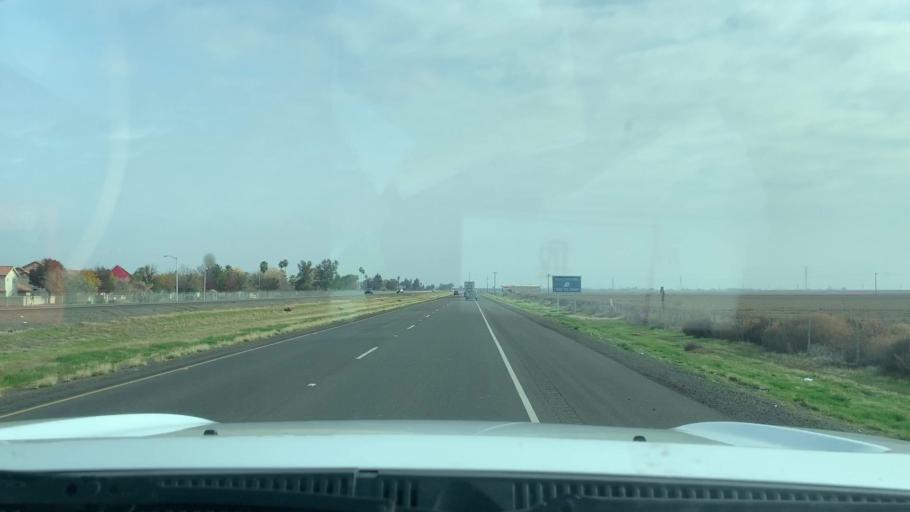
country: US
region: California
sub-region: Kings County
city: Lemoore Station
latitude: 36.2554
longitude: -119.8915
